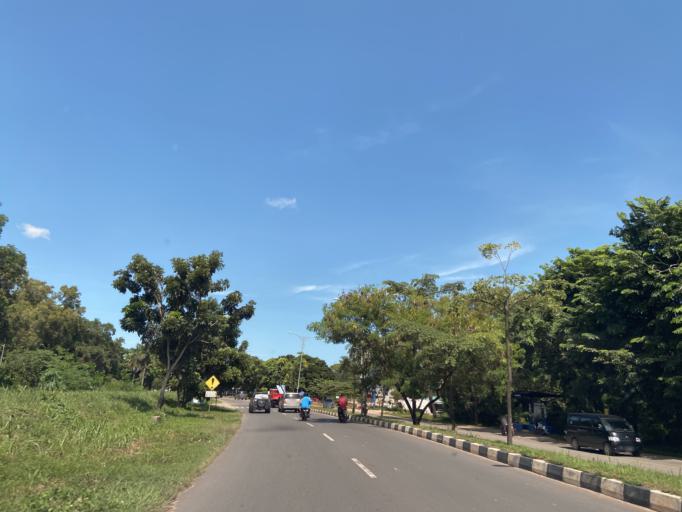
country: SG
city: Singapore
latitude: 1.1105
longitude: 104.0589
